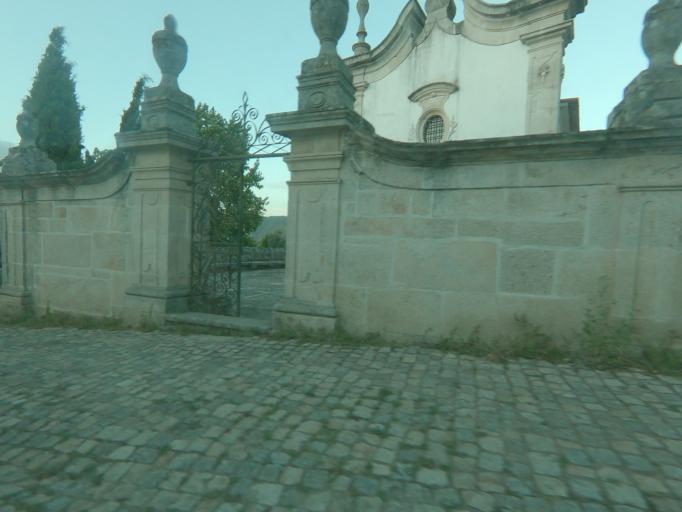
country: PT
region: Vila Real
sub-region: Peso da Regua
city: Peso da Regua
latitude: 41.1370
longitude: -7.7434
